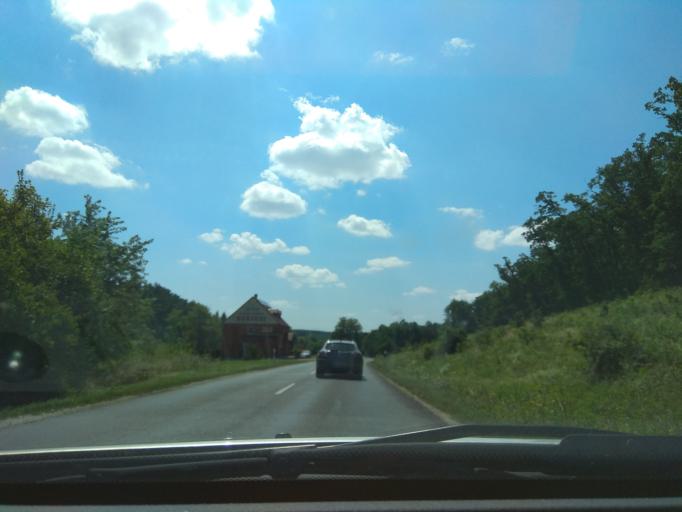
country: HU
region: Borsod-Abauj-Zemplen
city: Harsany
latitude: 48.0060
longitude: 20.7617
